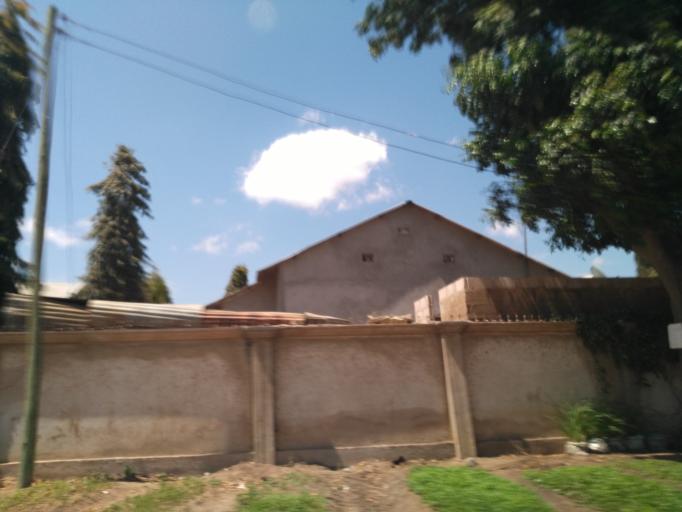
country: TZ
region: Dodoma
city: Kisasa
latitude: -6.1665
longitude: 35.7704
